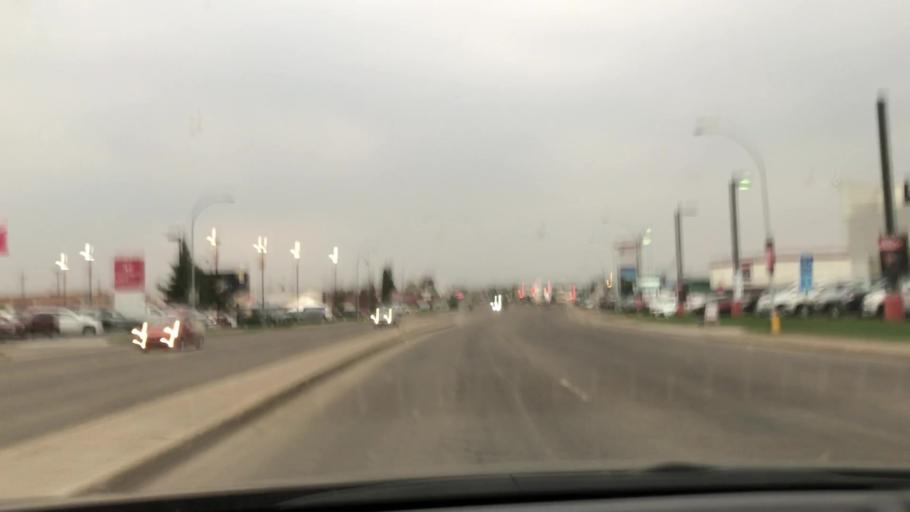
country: CA
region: Alberta
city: Edmonton
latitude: 53.4671
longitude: -113.4793
